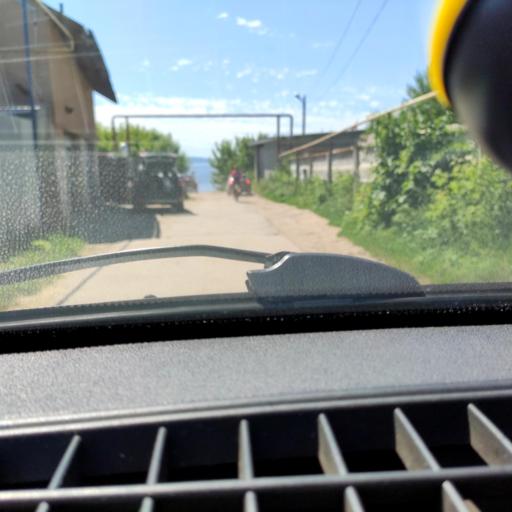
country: RU
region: Samara
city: Podstepki
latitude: 53.5102
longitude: 49.2284
